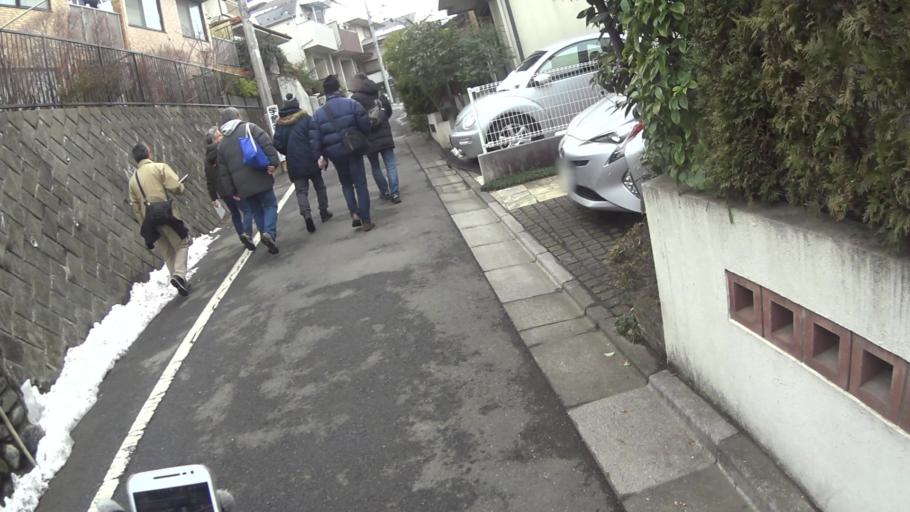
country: JP
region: Tokyo
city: Musashino
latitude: 35.7336
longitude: 139.5994
